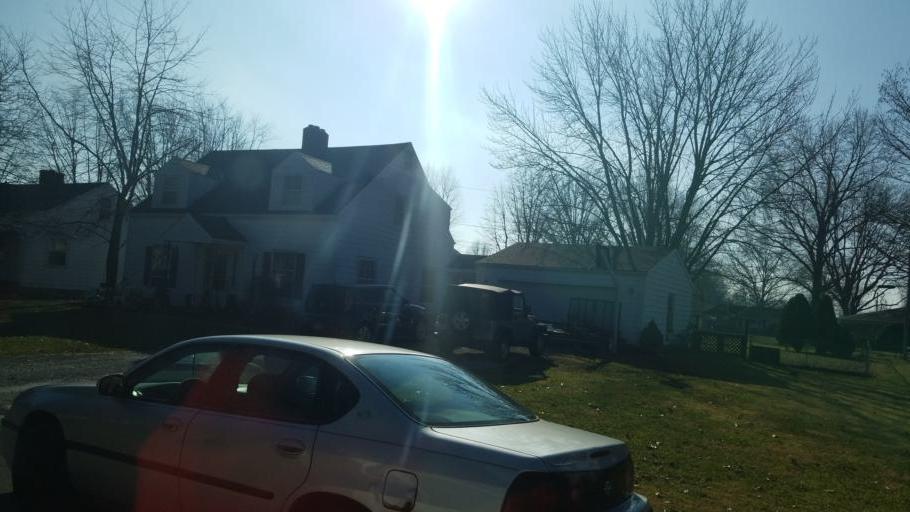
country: US
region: Ohio
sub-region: Seneca County
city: Tiffin
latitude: 41.1028
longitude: -83.1639
